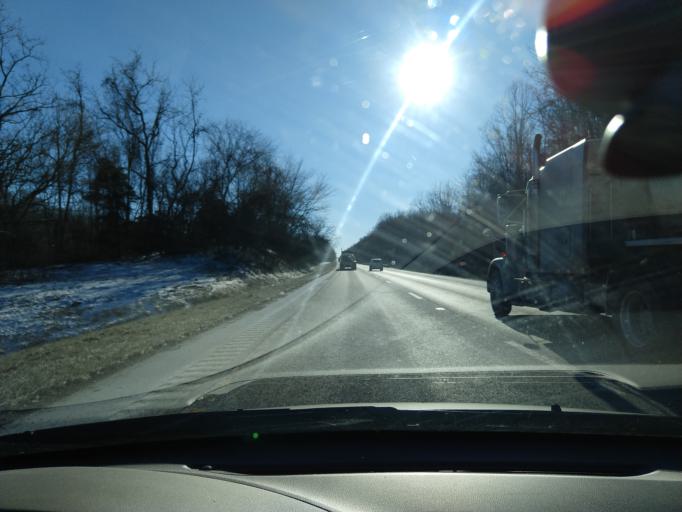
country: US
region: Virginia
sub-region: Botetourt County
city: Daleville
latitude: 37.4336
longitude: -79.8727
